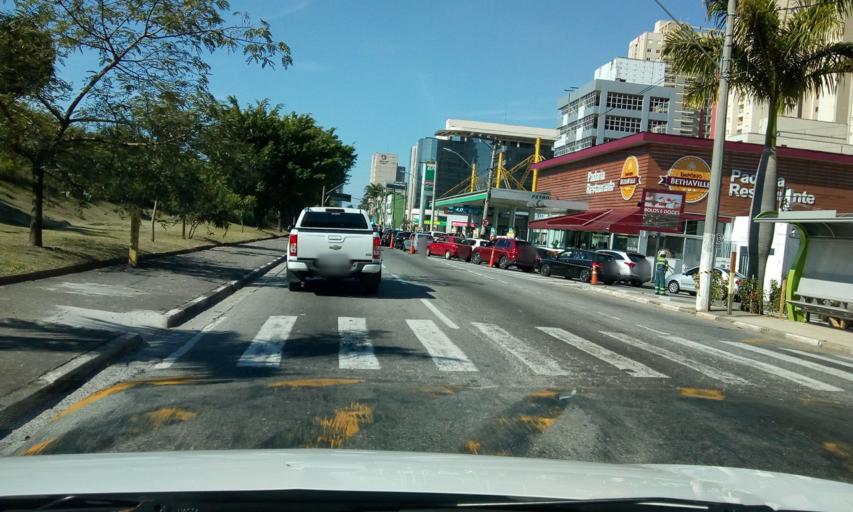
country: BR
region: Sao Paulo
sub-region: Barueri
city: Barueri
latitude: -23.5054
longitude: -46.8690
